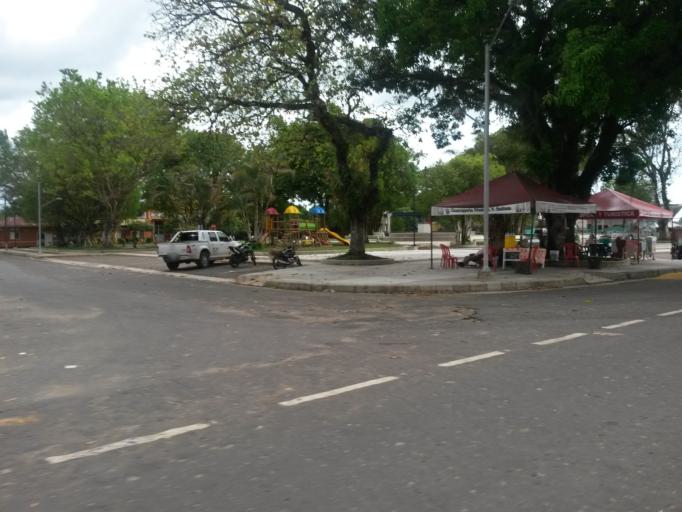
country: CO
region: Caqueta
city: Morelia
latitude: 1.4882
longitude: -75.7262
